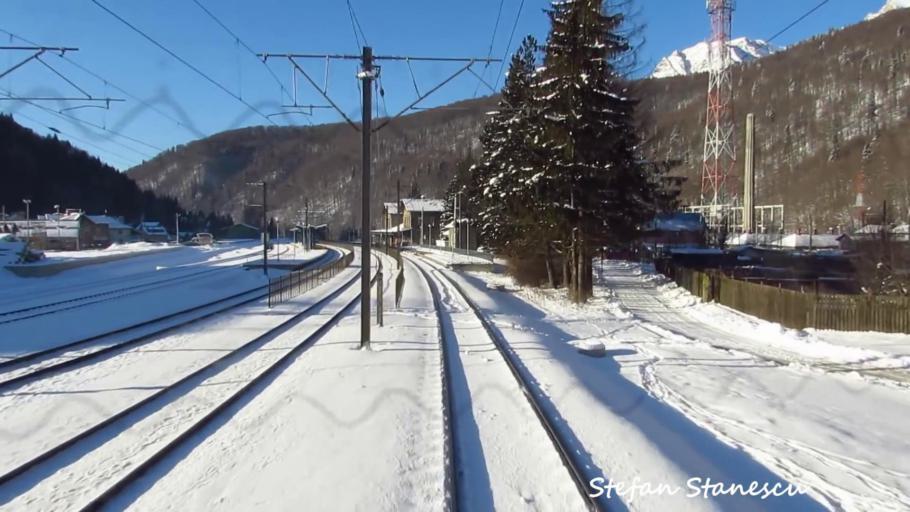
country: RO
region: Prahova
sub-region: Oras Azuga
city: Azuga
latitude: 45.4455
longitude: 25.5531
